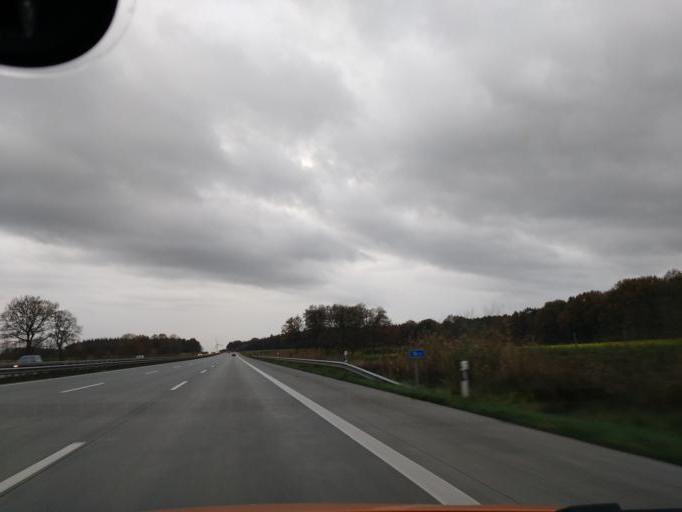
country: DE
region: Lower Saxony
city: Horstedt
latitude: 53.1646
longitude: 9.2444
